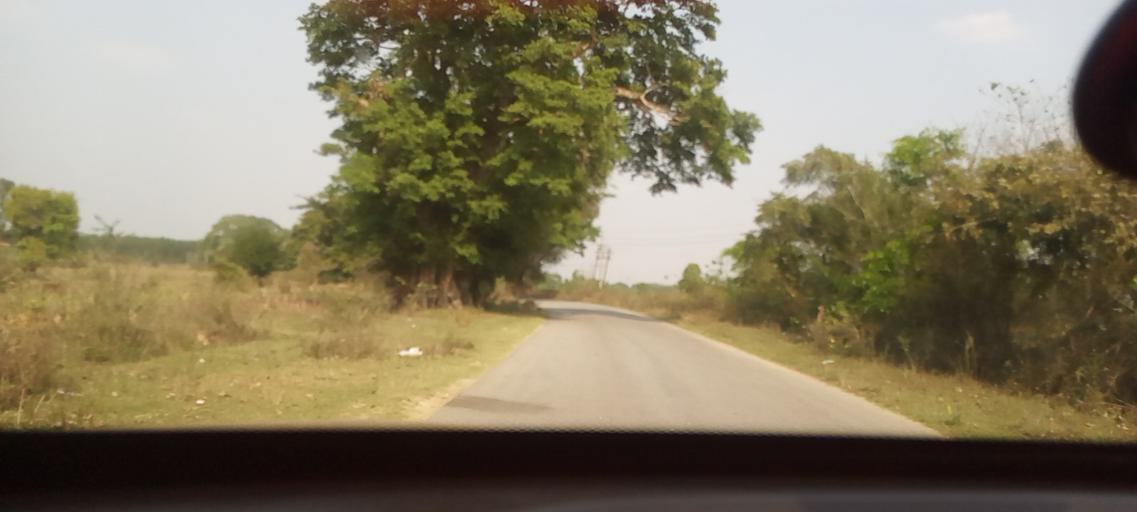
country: IN
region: Karnataka
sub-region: Hassan
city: Belur
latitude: 13.1749
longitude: 75.8175
